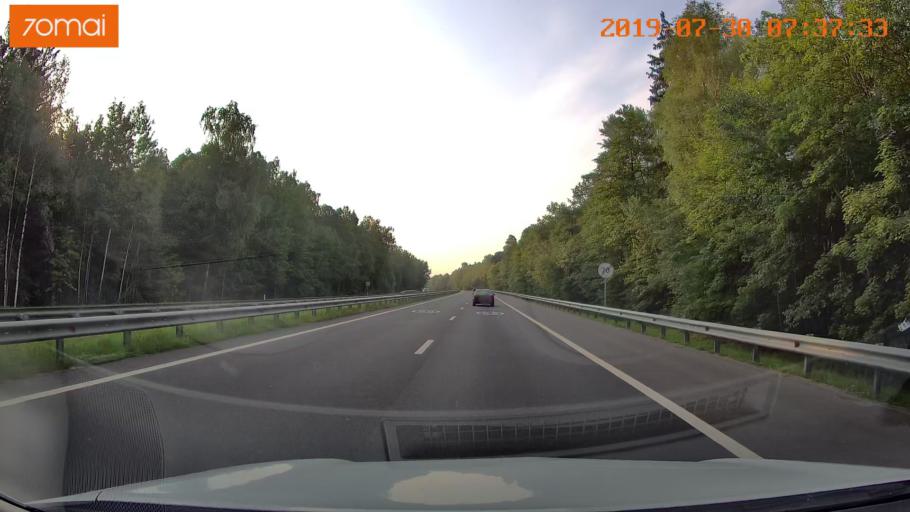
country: RU
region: Kaliningrad
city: Gvardeysk
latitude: 54.6551
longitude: 21.1480
